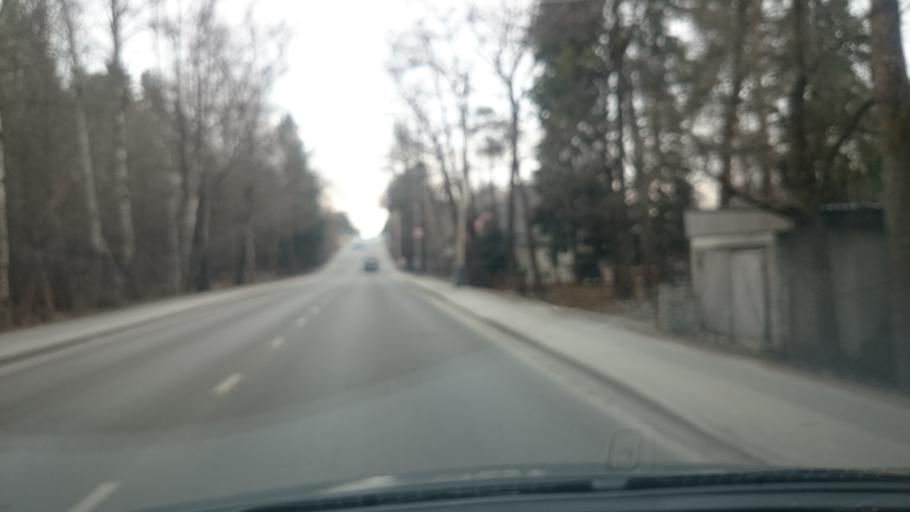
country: EE
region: Harju
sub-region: Saue vald
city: Laagri
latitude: 59.3891
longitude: 24.6415
